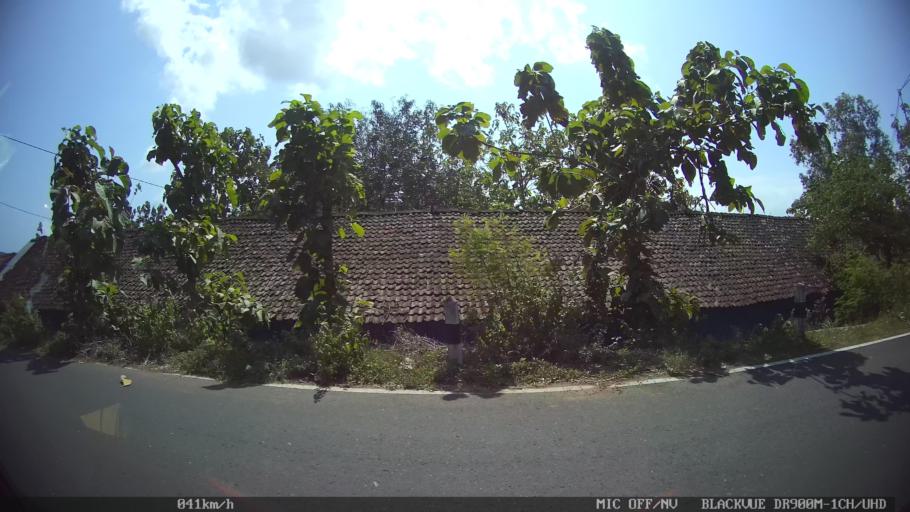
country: ID
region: Daerah Istimewa Yogyakarta
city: Pundong
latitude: -7.9750
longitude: 110.3477
